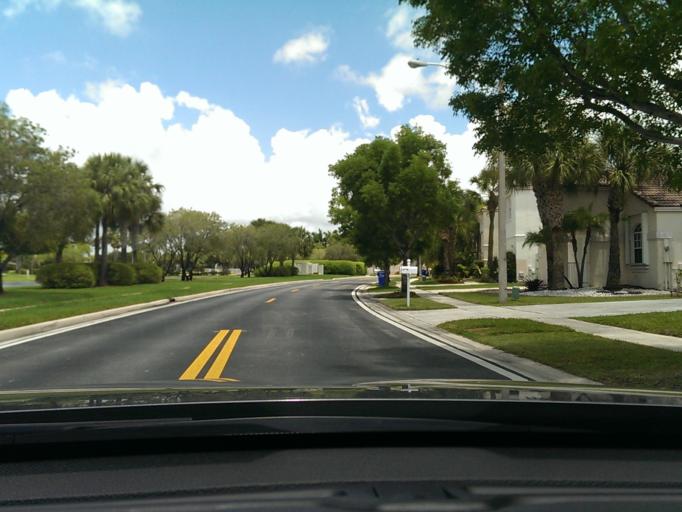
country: US
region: Florida
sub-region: Broward County
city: Sunshine Ranches
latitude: 26.0087
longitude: -80.3496
